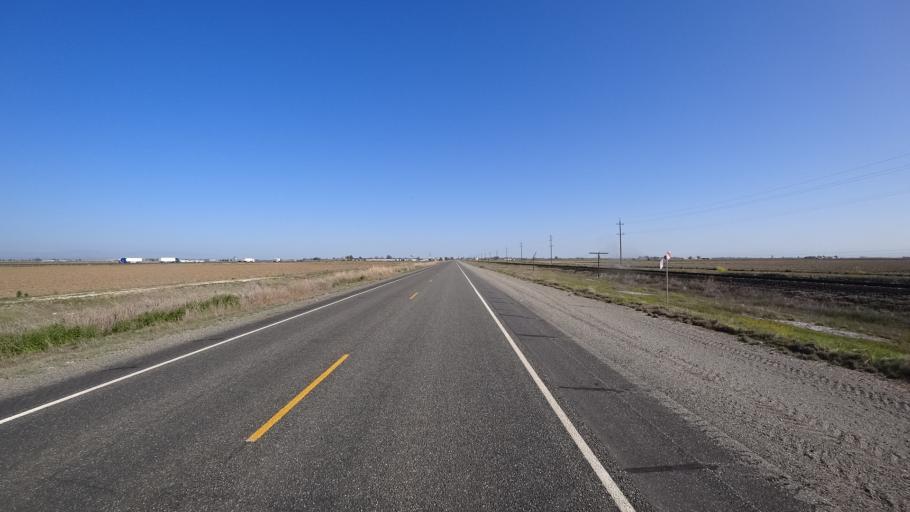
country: US
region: California
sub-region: Glenn County
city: Willows
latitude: 39.4837
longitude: -122.1931
